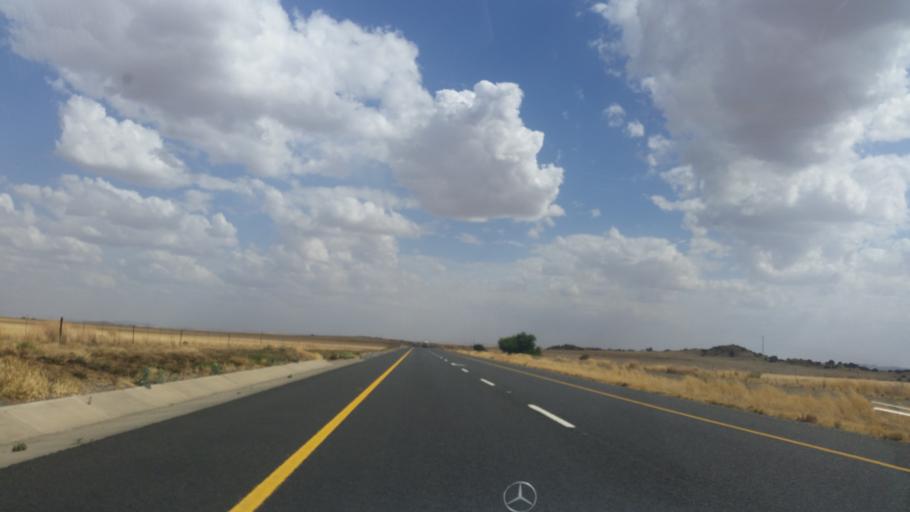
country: ZA
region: Orange Free State
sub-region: Mangaung Metropolitan Municipality
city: Bloemfontein
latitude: -29.5612
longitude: 26.0521
